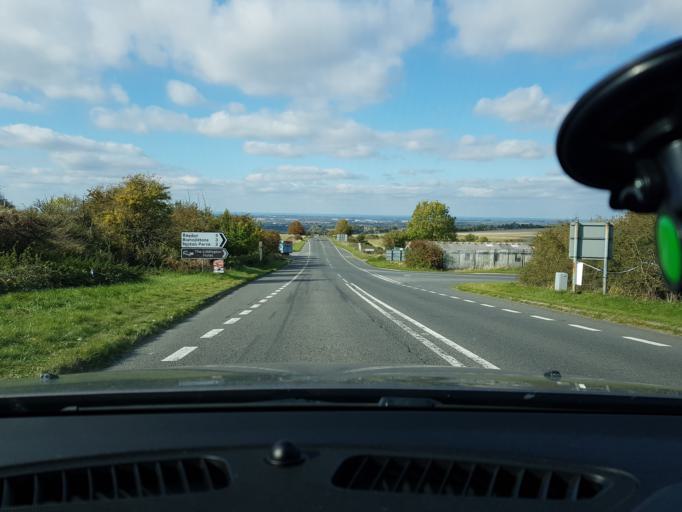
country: GB
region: England
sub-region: Borough of Swindon
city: Wanborough
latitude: 51.5233
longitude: -1.6875
